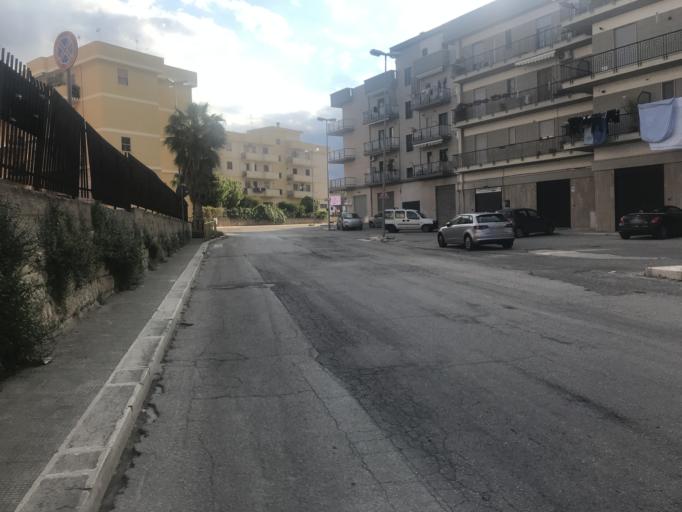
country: IT
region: Apulia
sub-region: Provincia di Bari
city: Corato
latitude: 41.1589
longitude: 16.4144
